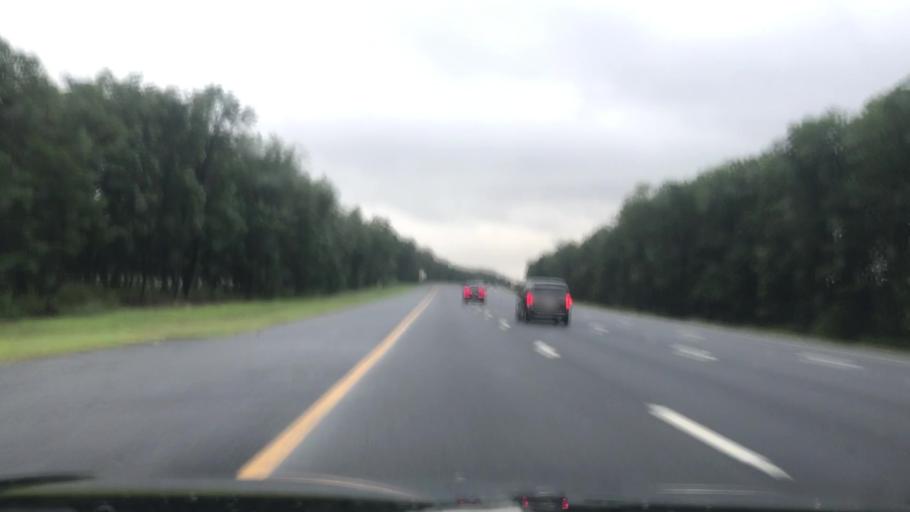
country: US
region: New Jersey
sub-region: Monmouth County
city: Ramtown
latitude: 40.1093
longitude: -74.1345
